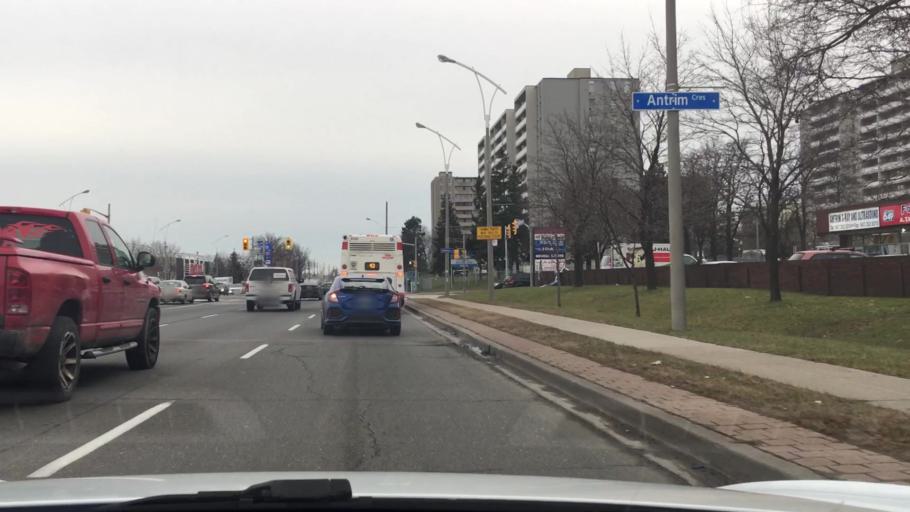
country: CA
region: Ontario
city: Scarborough
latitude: 43.7724
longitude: -79.2837
